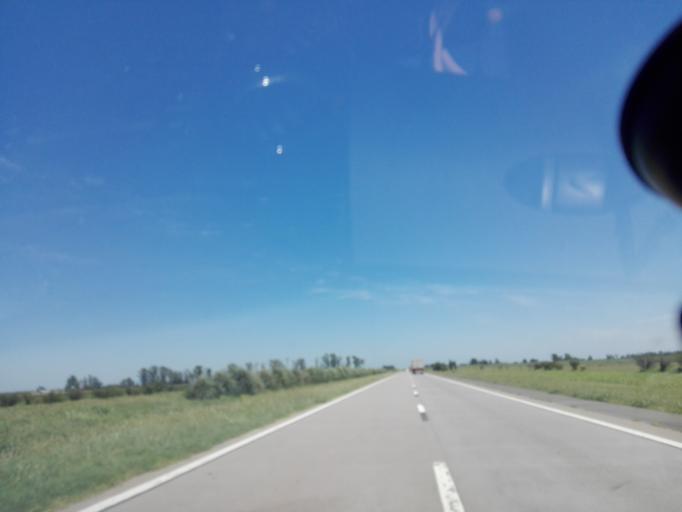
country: AR
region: Santa Fe
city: Armstrong
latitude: -32.7931
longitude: -61.7005
